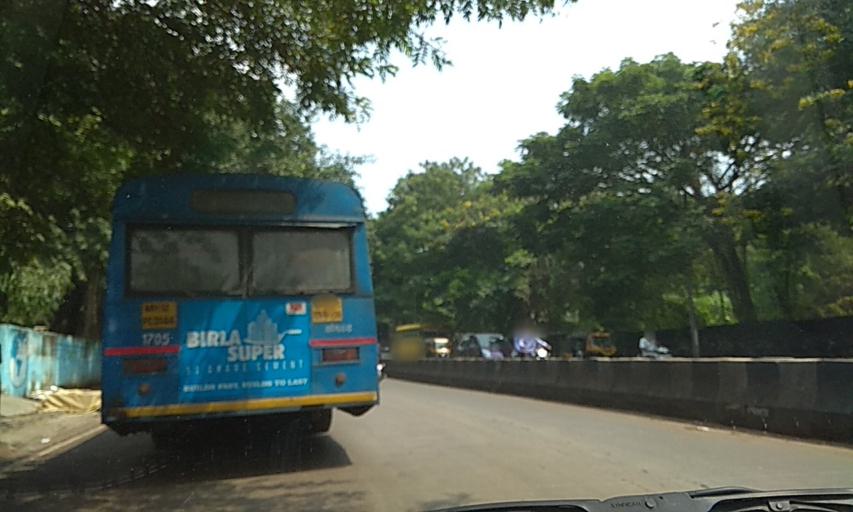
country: IN
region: Maharashtra
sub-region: Pune Division
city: Shivaji Nagar
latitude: 18.5372
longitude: 73.7942
